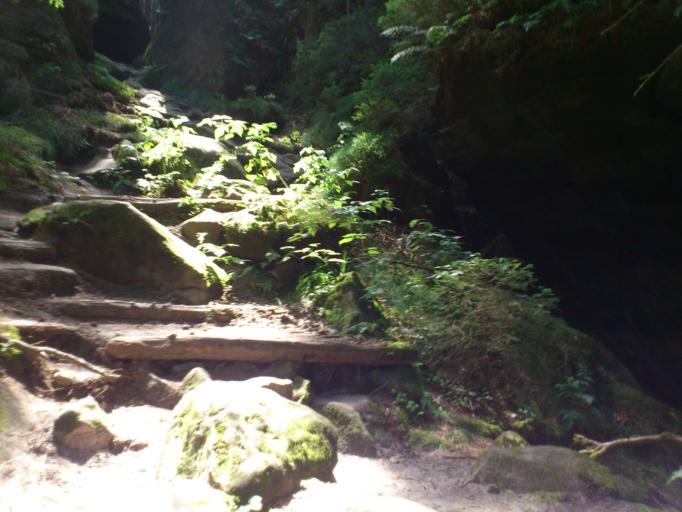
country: DE
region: Saxony
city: Sebnitz
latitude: 50.9223
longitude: 14.2855
